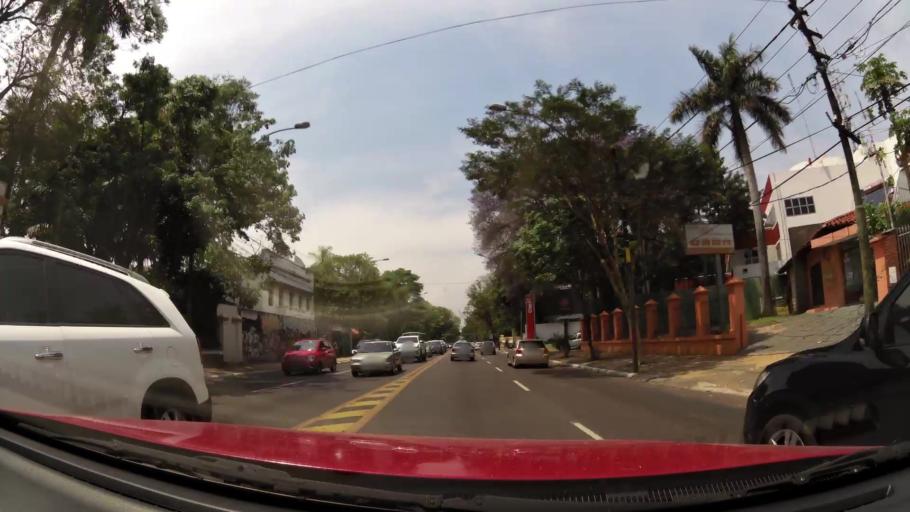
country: PY
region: Asuncion
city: Asuncion
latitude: -25.2929
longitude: -57.6056
